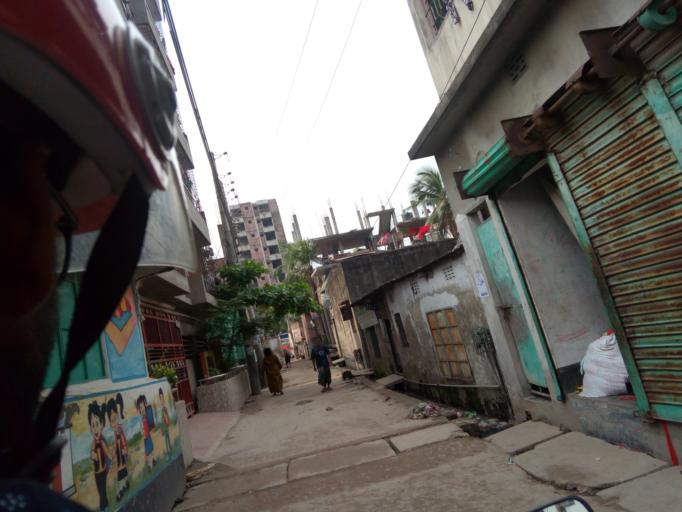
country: BD
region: Dhaka
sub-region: Dhaka
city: Dhaka
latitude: 23.7019
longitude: 90.4542
